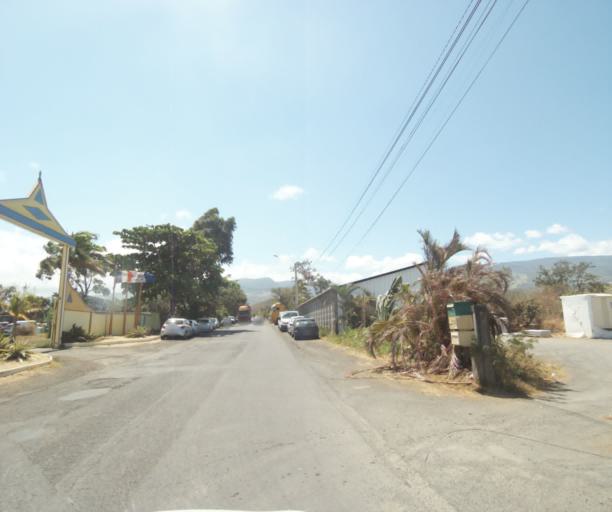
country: RE
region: Reunion
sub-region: Reunion
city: Le Port
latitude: -20.9613
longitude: 55.2989
